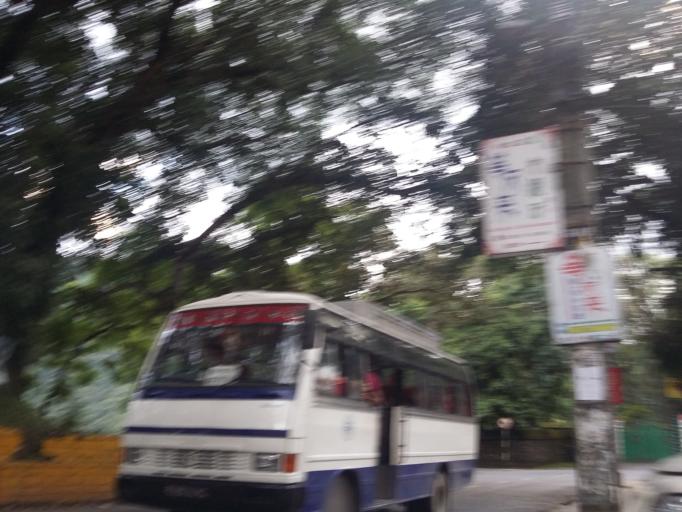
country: NP
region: Western Region
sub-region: Gandaki Zone
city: Pokhara
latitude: 28.2060
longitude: 83.9605
